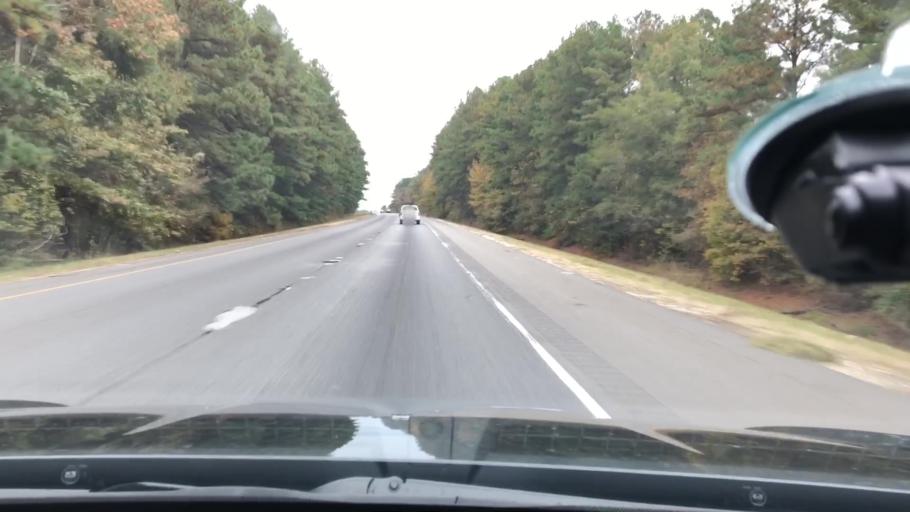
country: US
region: Arkansas
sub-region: Hot Spring County
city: Malvern
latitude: 34.3073
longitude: -92.9407
